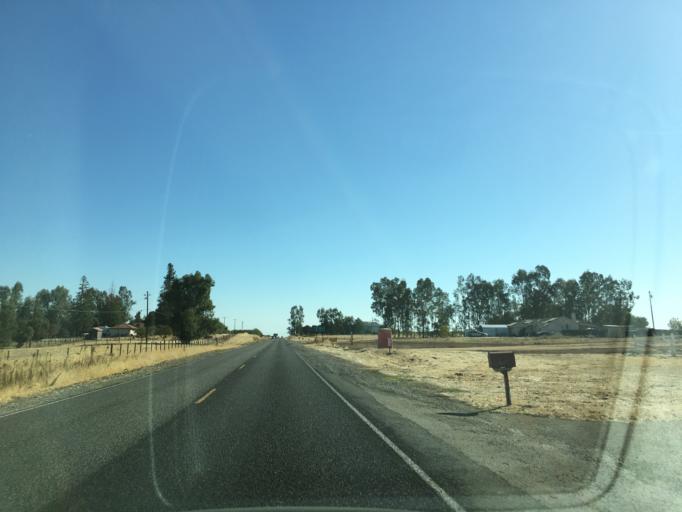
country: US
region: California
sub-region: Madera County
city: Parksdale
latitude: 36.9981
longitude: -119.9805
